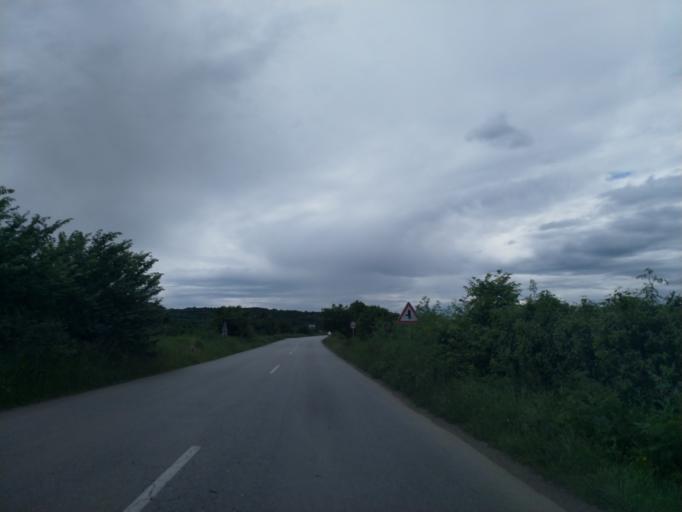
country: RS
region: Central Serbia
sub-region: Pomoravski Okrug
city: Jagodina
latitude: 43.9573
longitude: 21.2928
